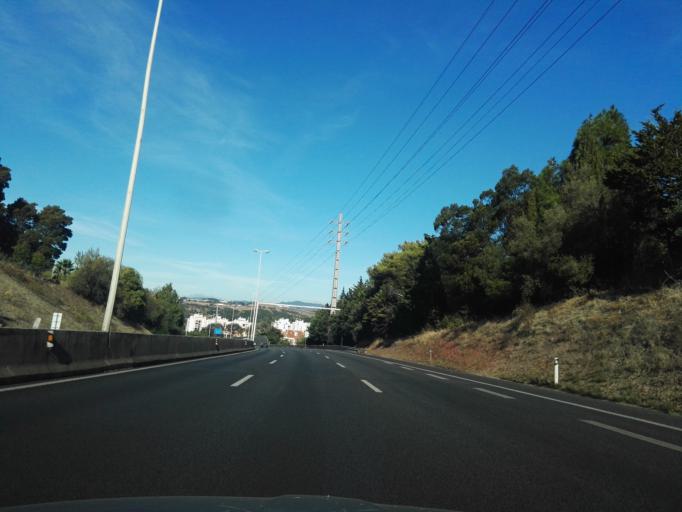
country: PT
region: Lisbon
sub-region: Oeiras
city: Linda-a-Velha
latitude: 38.7201
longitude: -9.2398
